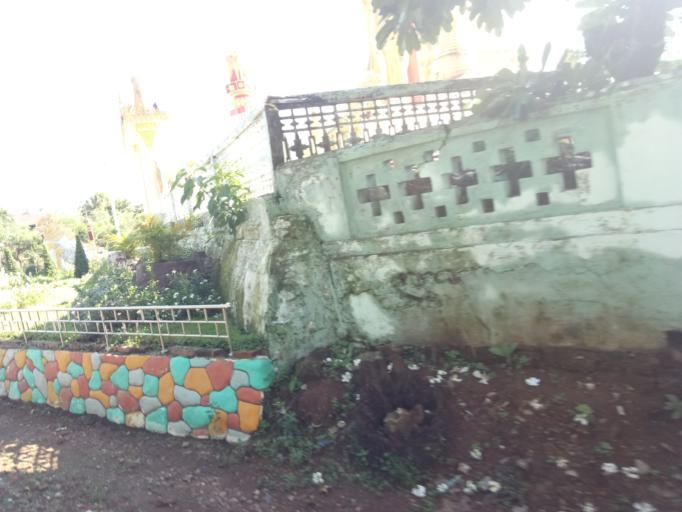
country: MM
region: Mon
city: Mawlamyine
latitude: 16.3568
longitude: 97.5570
